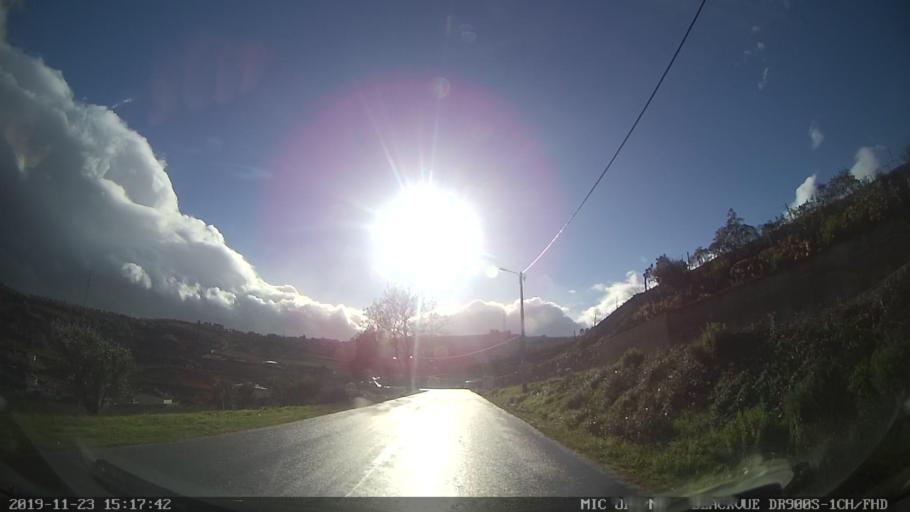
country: PT
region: Viseu
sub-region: Lamego
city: Lamego
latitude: 41.1227
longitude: -7.7929
